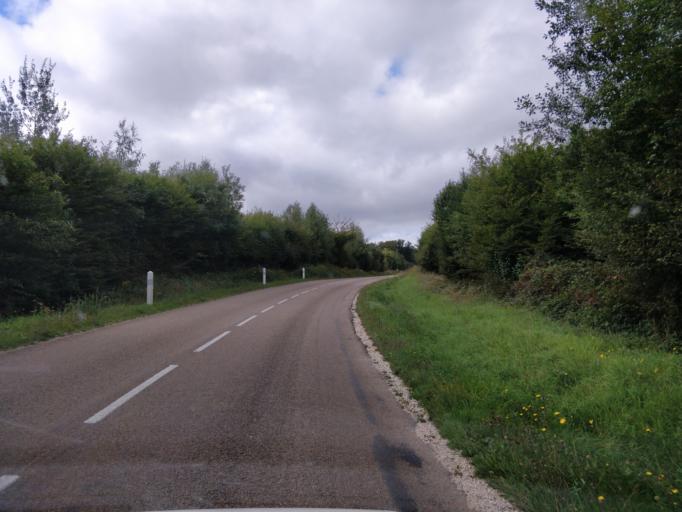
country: FR
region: Bourgogne
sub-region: Departement de l'Yonne
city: Saint-Florentin
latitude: 48.0991
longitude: 3.6784
